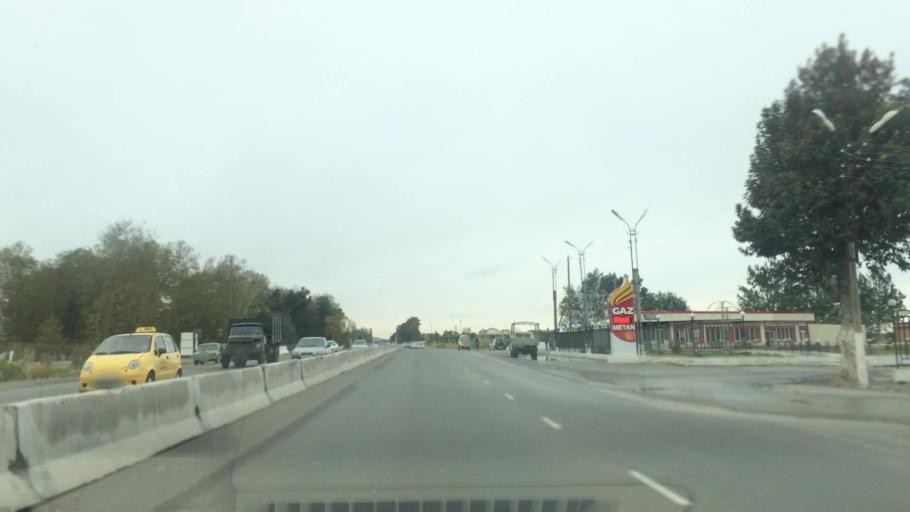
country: UZ
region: Samarqand
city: Jomboy
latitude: 39.7202
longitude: 67.1188
